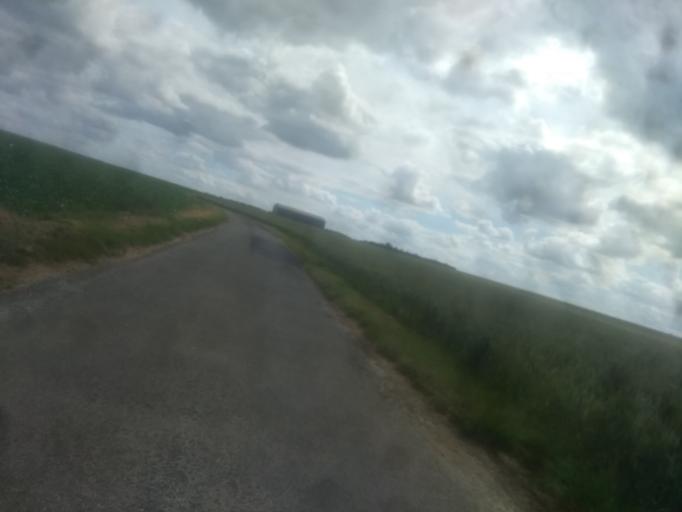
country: FR
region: Nord-Pas-de-Calais
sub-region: Departement du Pas-de-Calais
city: Duisans
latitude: 50.2967
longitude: 2.6940
